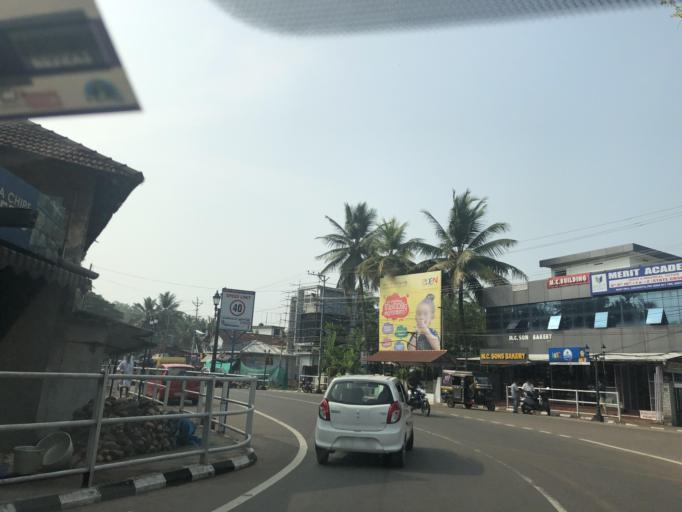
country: IN
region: Kerala
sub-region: Kozhikode
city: Kozhikode
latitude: 11.2902
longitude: 75.7753
